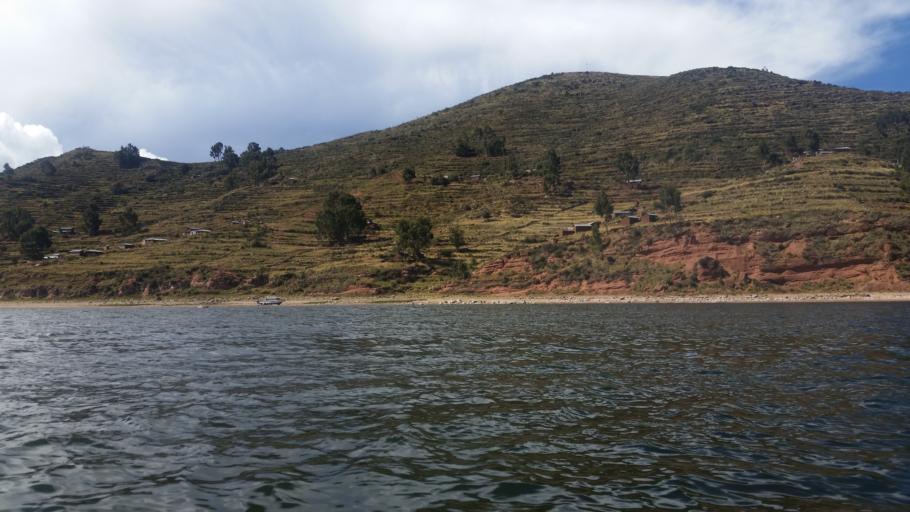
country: PE
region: Puno
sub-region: Provincia de Puno
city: Taquile
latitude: -15.7302
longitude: -69.7595
